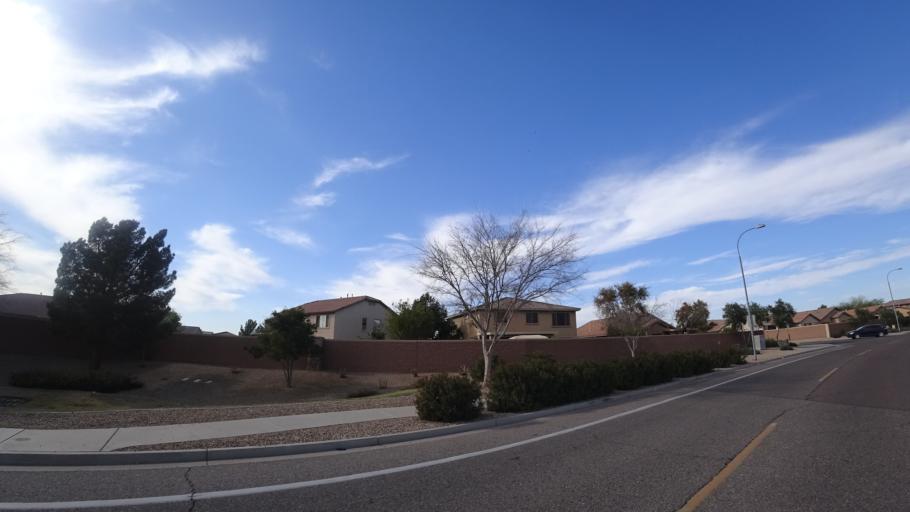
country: US
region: Arizona
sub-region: Maricopa County
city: Tolleson
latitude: 33.4155
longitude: -112.2817
